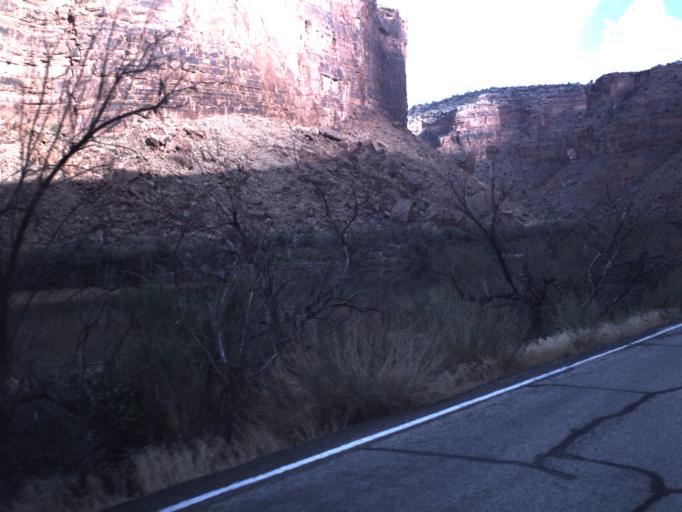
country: US
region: Utah
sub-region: Grand County
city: Moab
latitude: 38.8005
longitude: -109.3336
